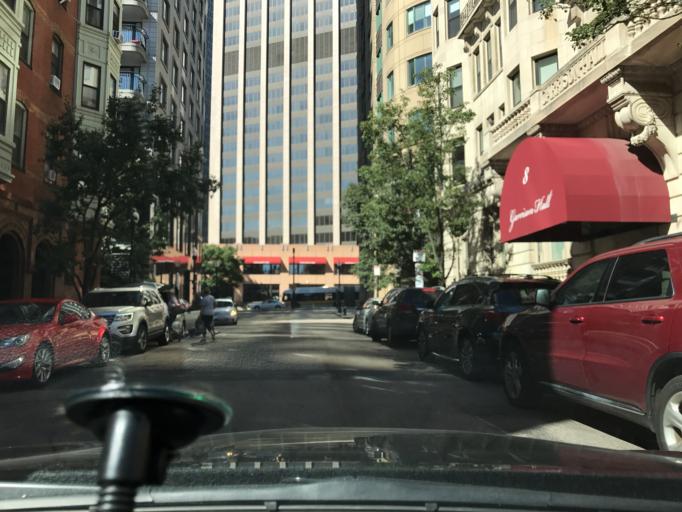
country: US
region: Massachusetts
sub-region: Suffolk County
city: Boston
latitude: 42.3460
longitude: -71.0797
